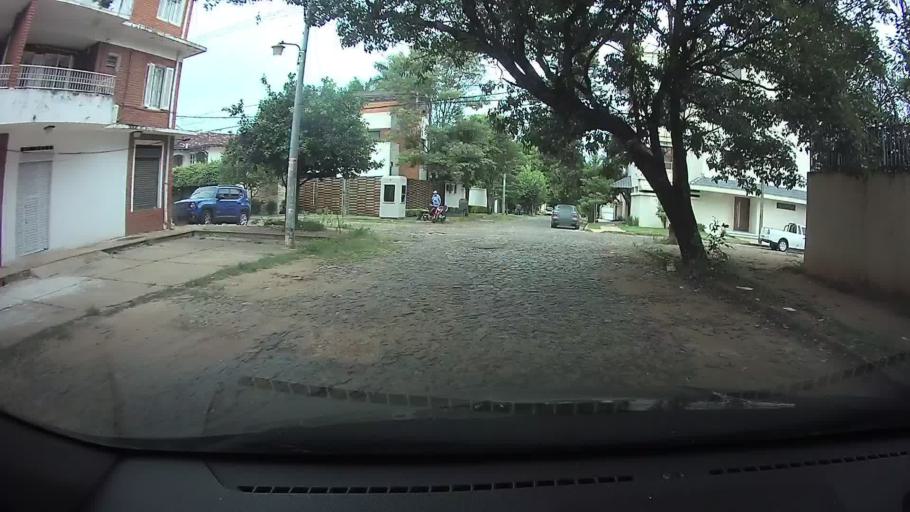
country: PY
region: Asuncion
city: Asuncion
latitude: -25.2786
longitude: -57.5720
